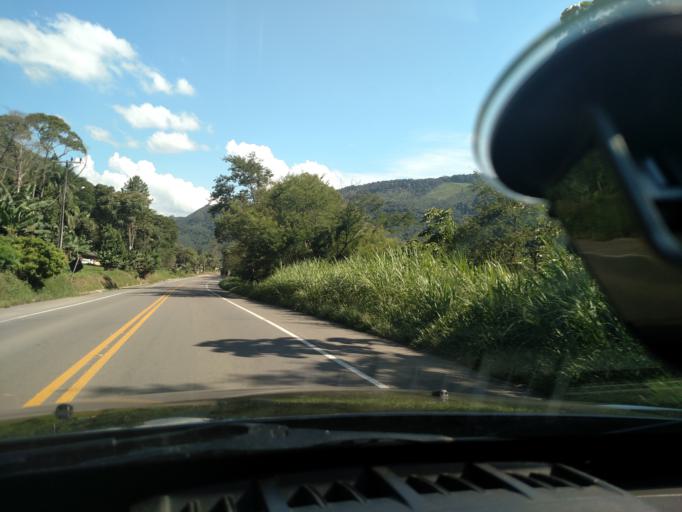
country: BR
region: Santa Catarina
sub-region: Ibirama
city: Ibirama
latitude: -27.0922
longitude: -49.4579
